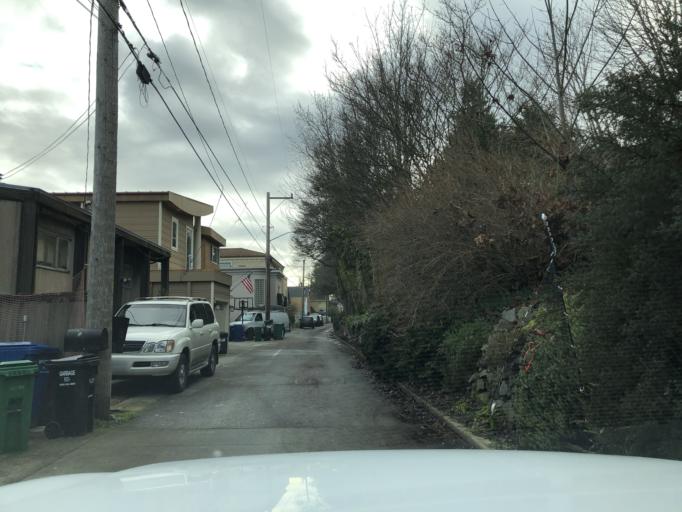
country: US
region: Washington
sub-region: King County
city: Lake Forest Park
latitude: 47.7135
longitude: -122.2772
